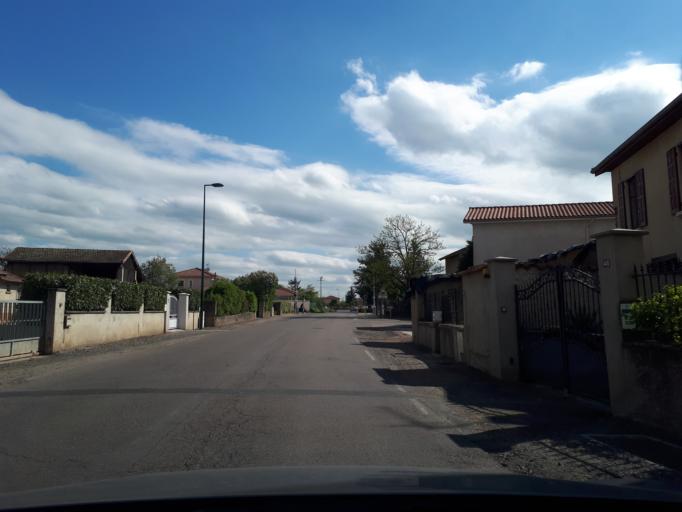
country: FR
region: Rhone-Alpes
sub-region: Departement de la Loire
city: Bellegarde-en-Forez
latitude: 45.6434
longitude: 4.2984
